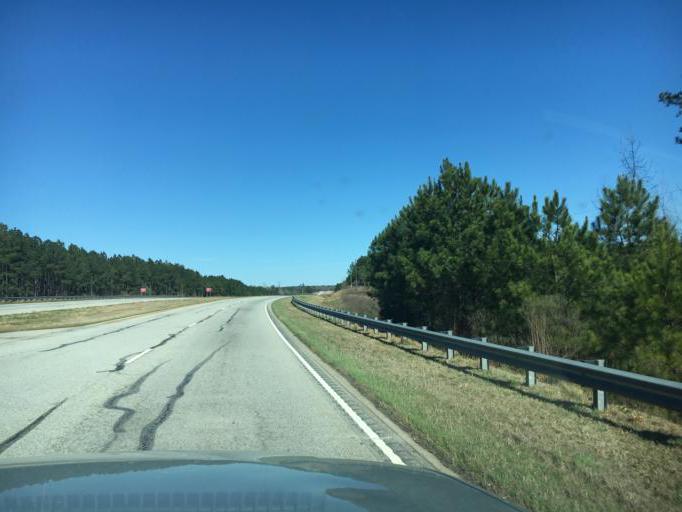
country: US
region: South Carolina
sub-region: Laurens County
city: Laurens
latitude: 34.3377
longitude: -81.9818
